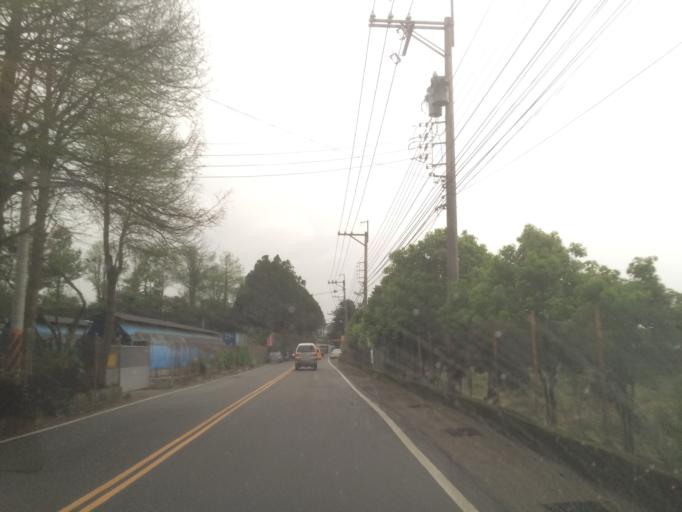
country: TW
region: Taiwan
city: Fengyuan
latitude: 24.1866
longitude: 120.8147
